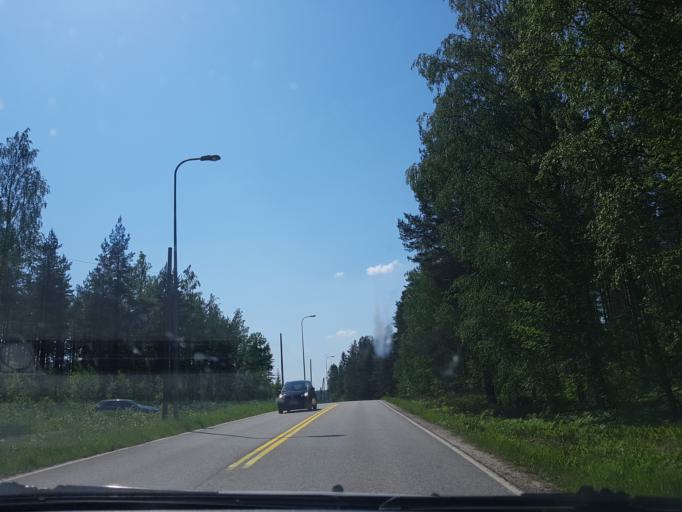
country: FI
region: Uusimaa
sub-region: Helsinki
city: Vihti
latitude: 60.3331
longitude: 24.4287
